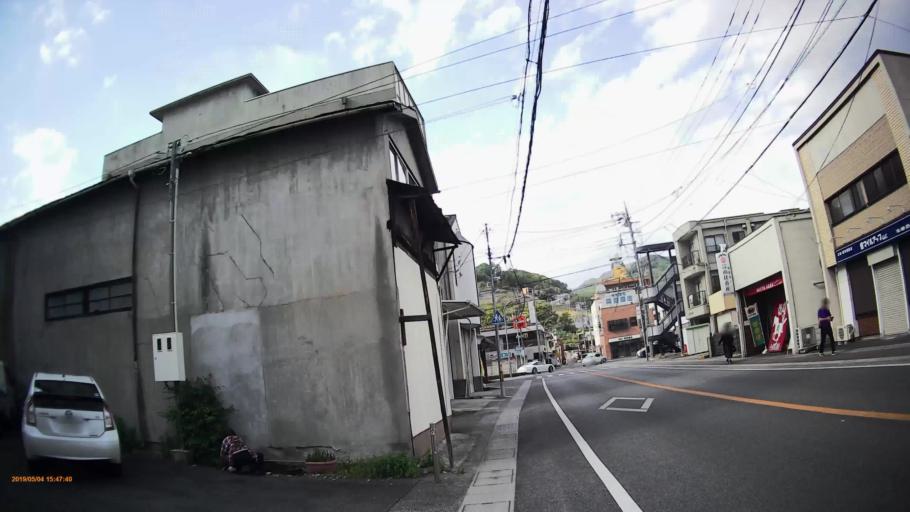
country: JP
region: Yamanashi
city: Kofu-shi
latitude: 35.6604
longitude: 138.5788
